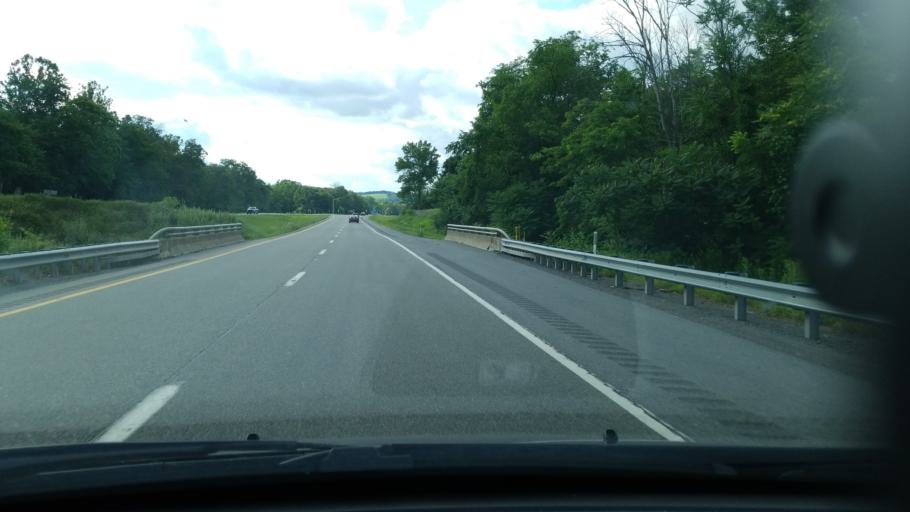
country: US
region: Pennsylvania
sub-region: Montour County
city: Danville
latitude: 40.9833
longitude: -76.6284
